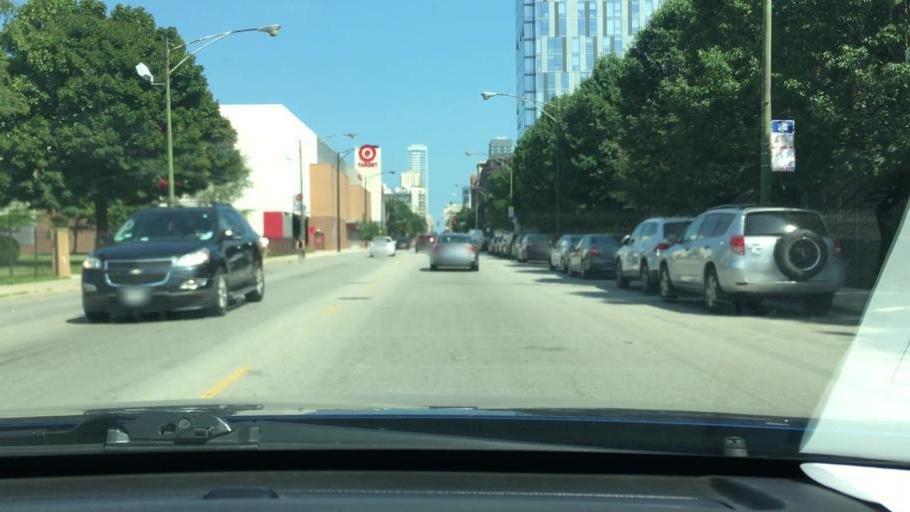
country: US
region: Illinois
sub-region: Cook County
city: Chicago
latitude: 41.9036
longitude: -87.6462
